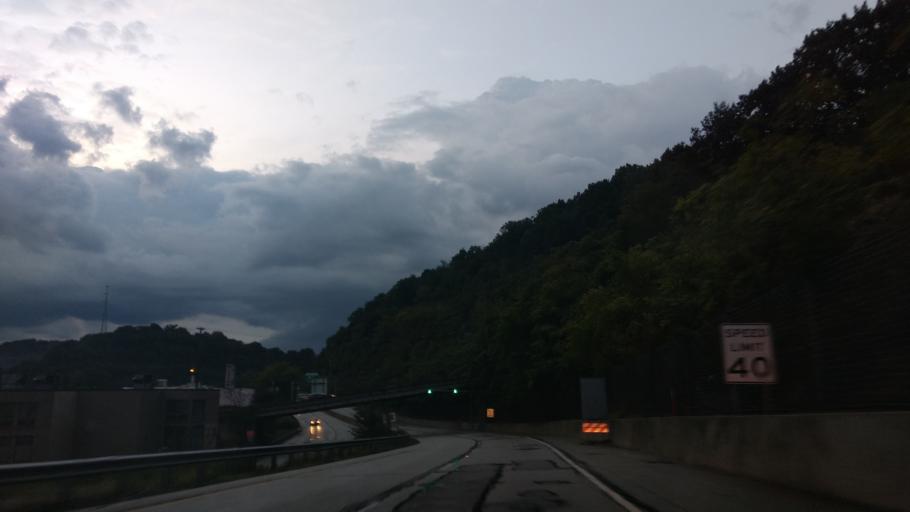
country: US
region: Pennsylvania
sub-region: Allegheny County
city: Green Tree
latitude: 40.4327
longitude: -80.0278
